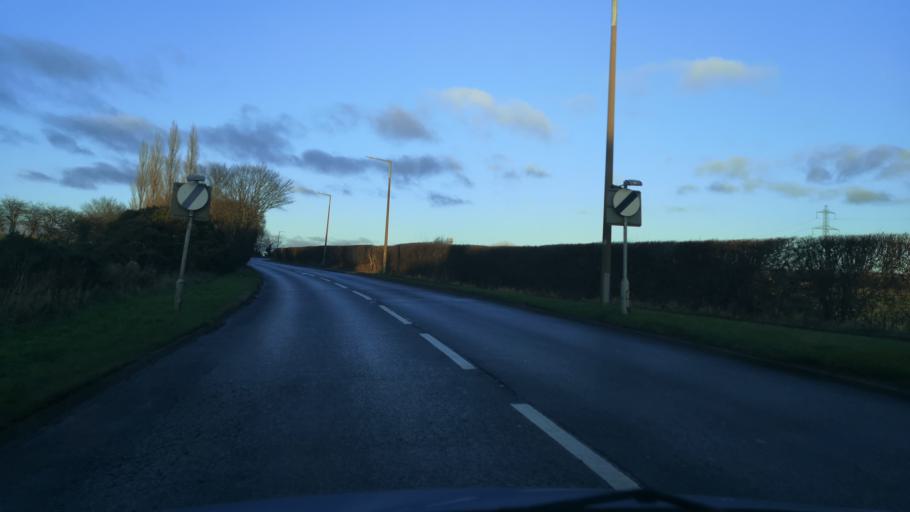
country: GB
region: England
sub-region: Barnsley
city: Little Houghton
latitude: 53.5414
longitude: -1.3494
